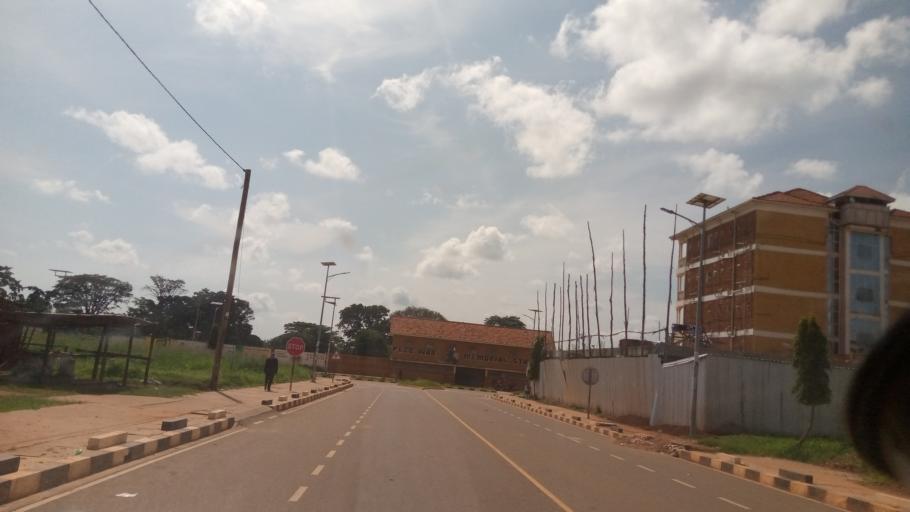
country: UG
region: Northern Region
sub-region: Gulu District
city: Gulu
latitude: 2.7701
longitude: 32.3077
